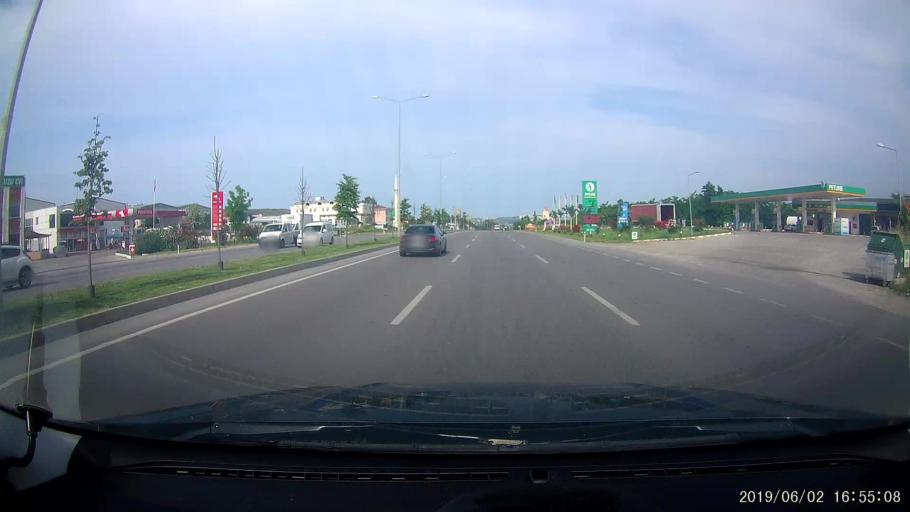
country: TR
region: Samsun
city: Samsun
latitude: 41.2926
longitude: 36.2468
